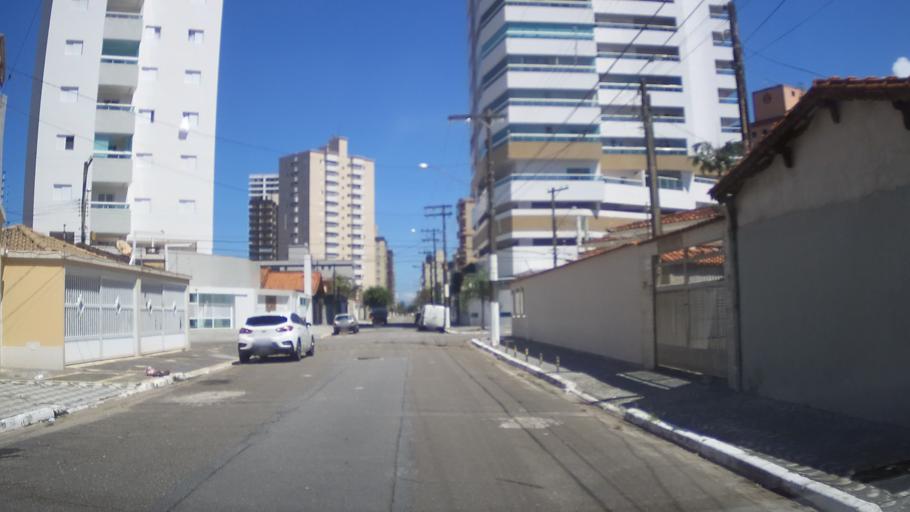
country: BR
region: Sao Paulo
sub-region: Mongagua
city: Mongagua
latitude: -24.0482
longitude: -46.5241
